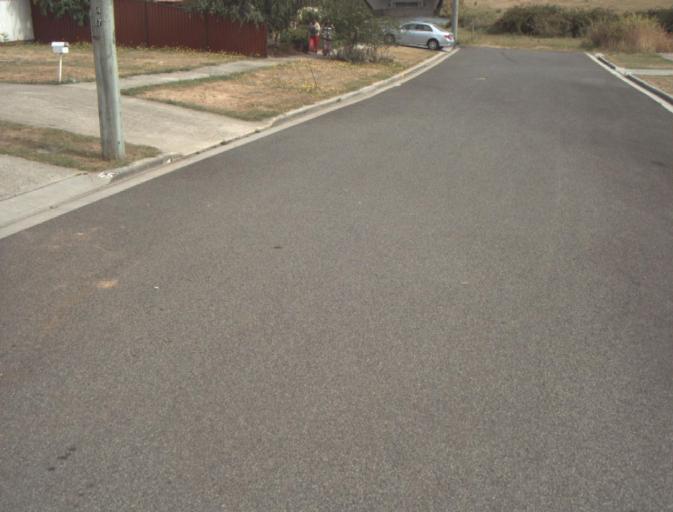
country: AU
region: Tasmania
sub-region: Launceston
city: Mayfield
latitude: -41.3856
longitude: 147.1105
